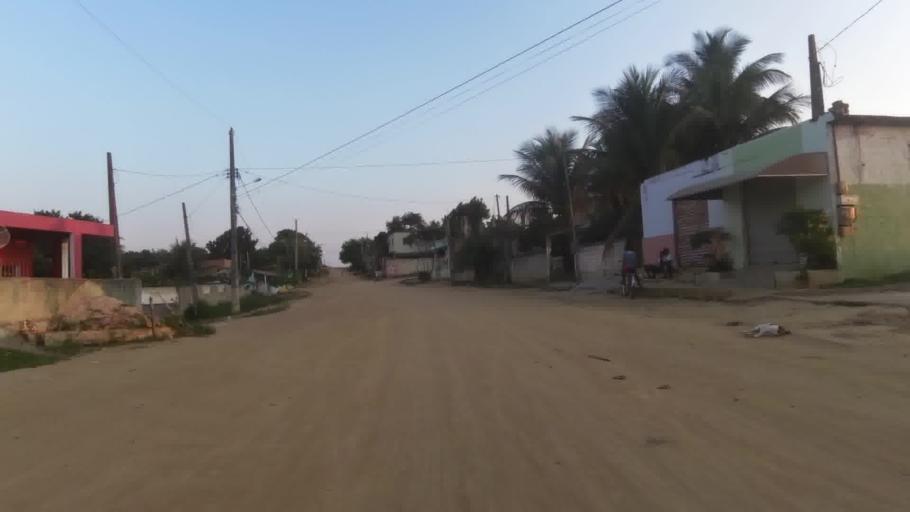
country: BR
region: Espirito Santo
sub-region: Piuma
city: Piuma
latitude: -20.8232
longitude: -40.7205
